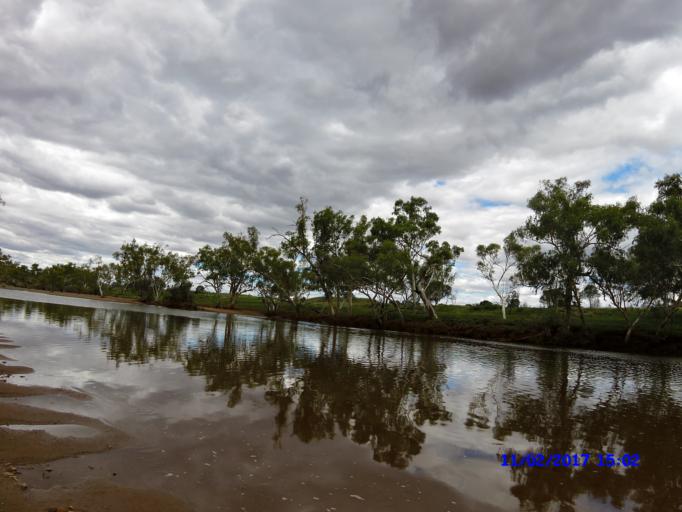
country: AU
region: Western Australia
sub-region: Ashburton
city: Tom Price
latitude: -23.1052
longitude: 118.0637
